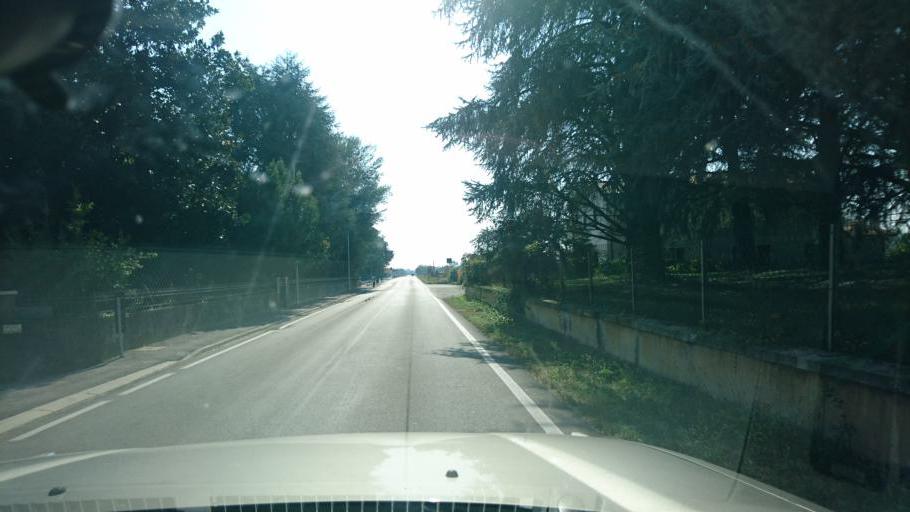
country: IT
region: Veneto
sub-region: Provincia di Padova
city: Gazzo
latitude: 45.5790
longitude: 11.7082
